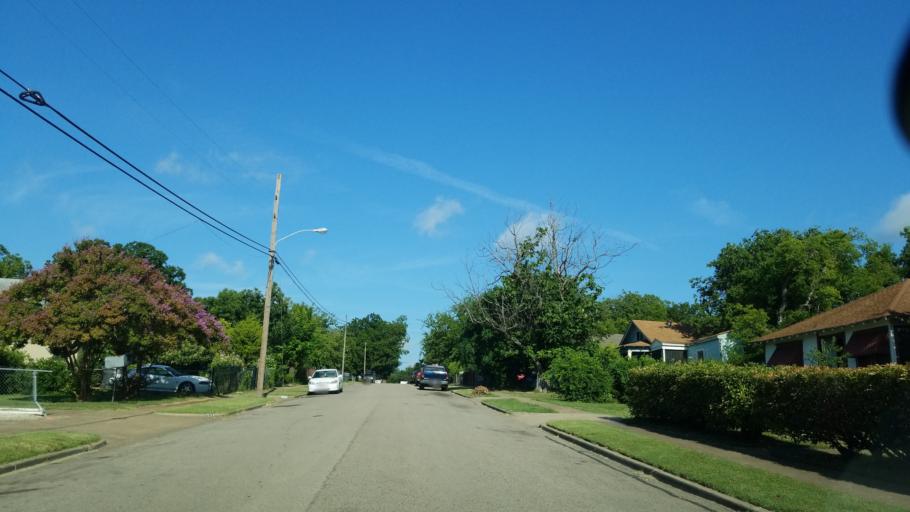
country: US
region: Texas
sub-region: Dallas County
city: Dallas
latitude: 32.7257
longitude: -96.8017
